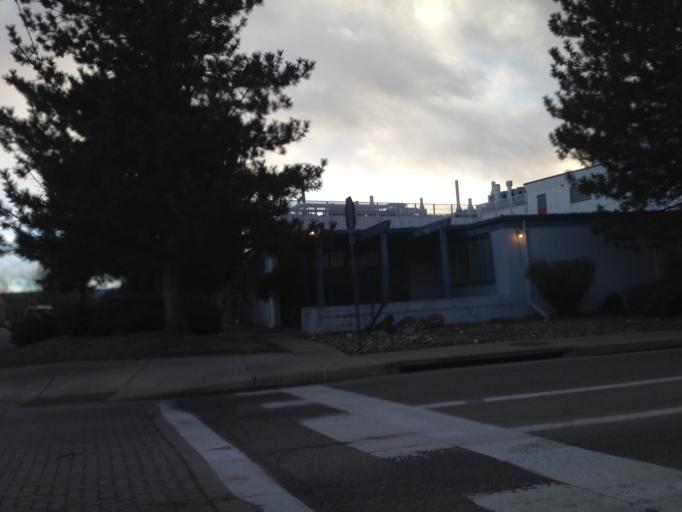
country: US
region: Colorado
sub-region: Boulder County
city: Boulder
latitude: 40.0200
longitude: -105.2497
